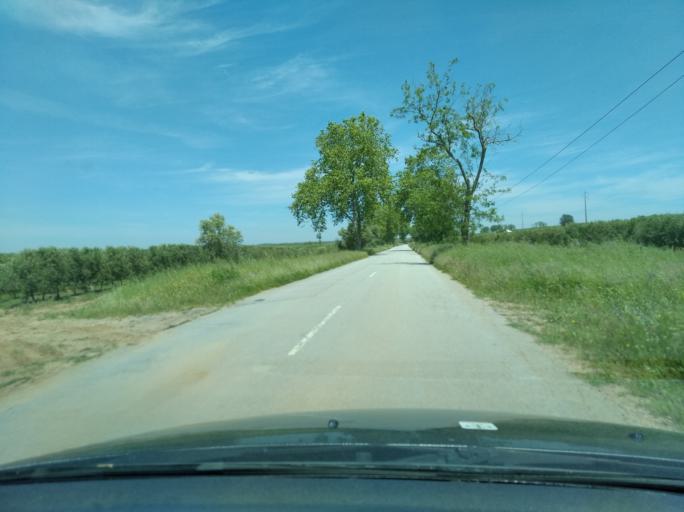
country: PT
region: Portalegre
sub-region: Avis
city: Avis
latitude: 39.0760
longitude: -7.8812
